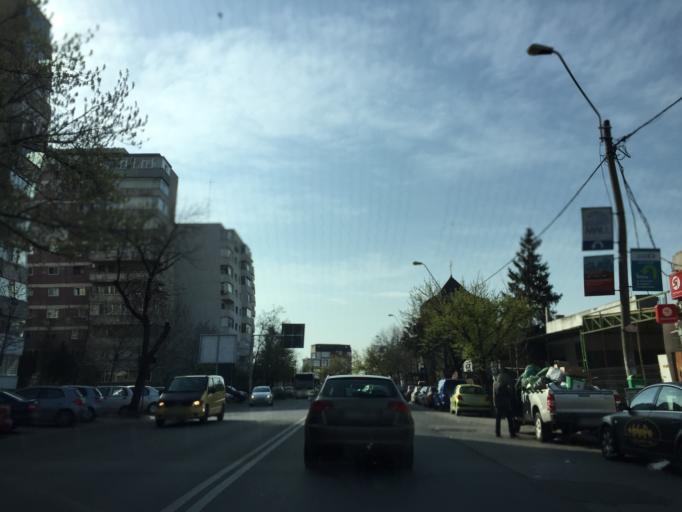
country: RO
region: Bucuresti
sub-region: Municipiul Bucuresti
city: Bucharest
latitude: 44.4144
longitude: 26.1330
